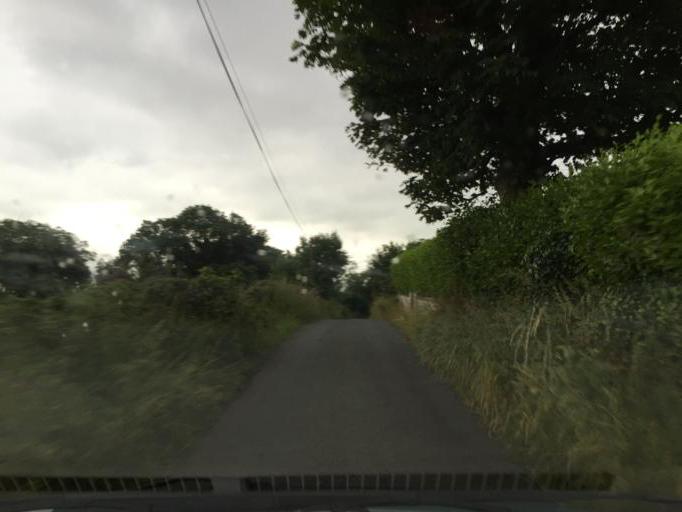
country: IE
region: Connaught
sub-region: Sligo
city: Strandhill
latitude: 54.2482
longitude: -8.5715
